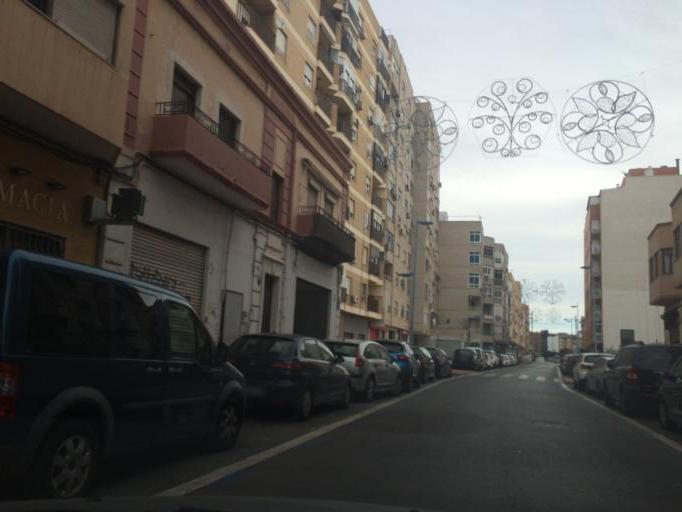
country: ES
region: Andalusia
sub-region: Provincia de Almeria
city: Almeria
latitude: 36.8371
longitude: -2.4546
